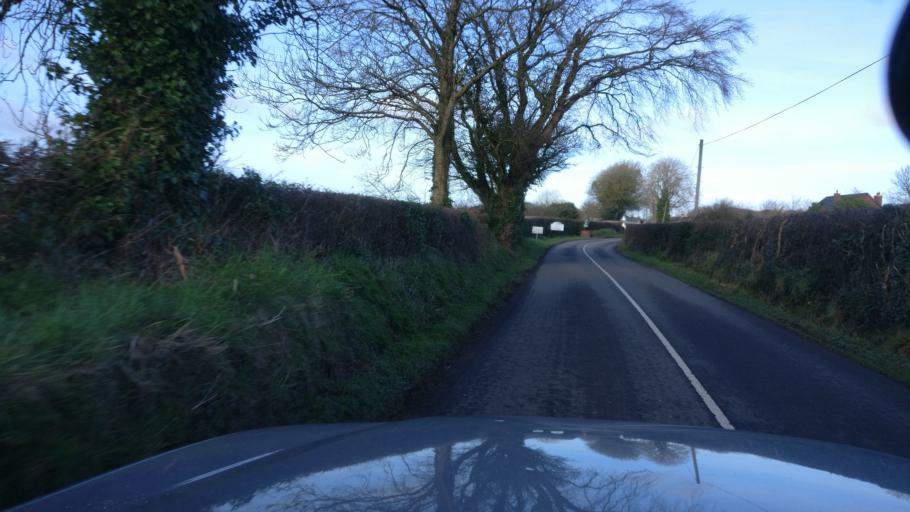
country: IE
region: Leinster
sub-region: Kilkenny
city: Castlecomer
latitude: 52.8868
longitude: -7.1611
